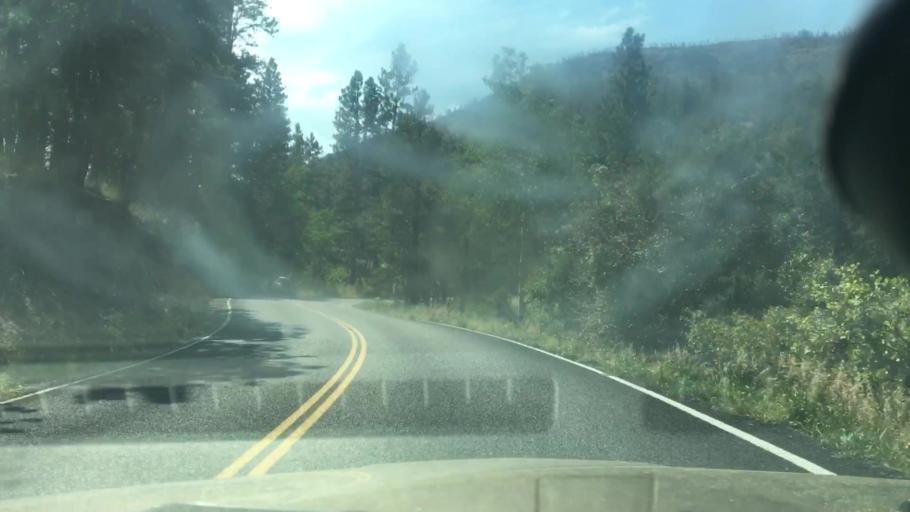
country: US
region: Colorado
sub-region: Larimer County
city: Laporte
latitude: 40.6664
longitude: -105.3819
